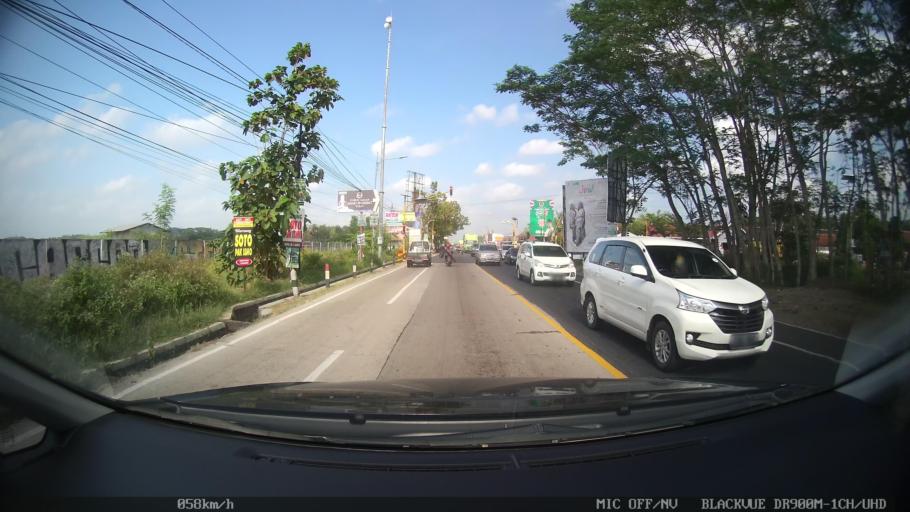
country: ID
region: Daerah Istimewa Yogyakarta
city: Godean
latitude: -7.8201
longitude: 110.2409
